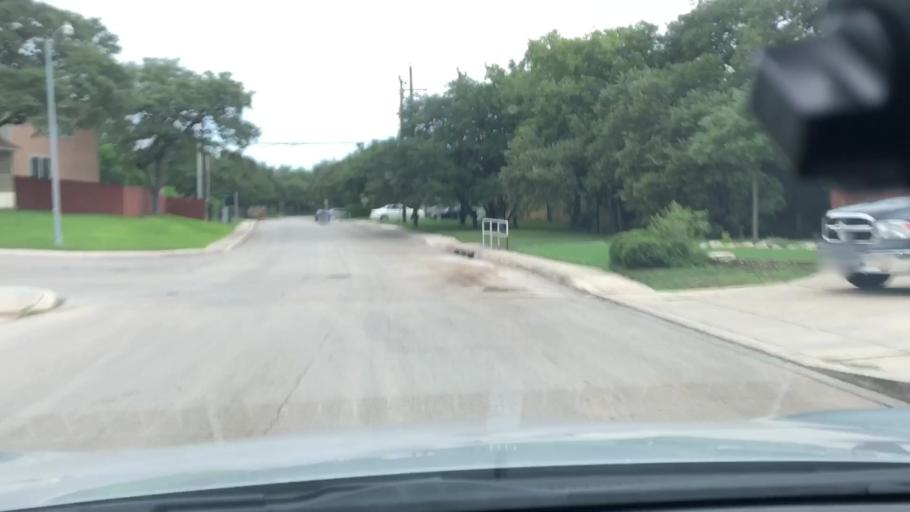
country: US
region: Texas
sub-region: Bexar County
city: Leon Valley
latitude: 29.5034
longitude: -98.6698
